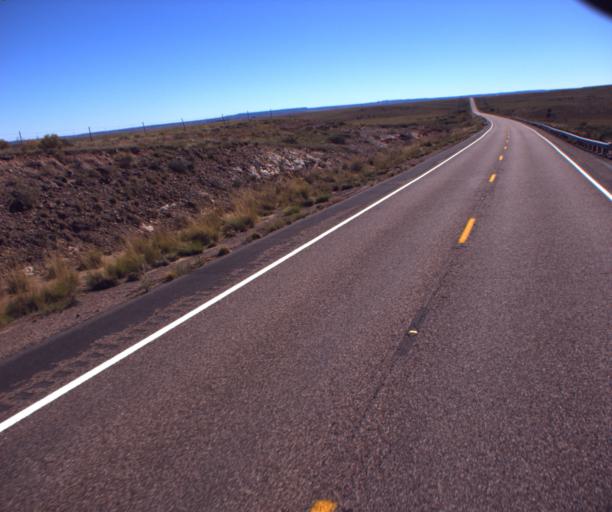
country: US
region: Arizona
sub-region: Apache County
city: Saint Johns
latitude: 34.5511
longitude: -109.4877
